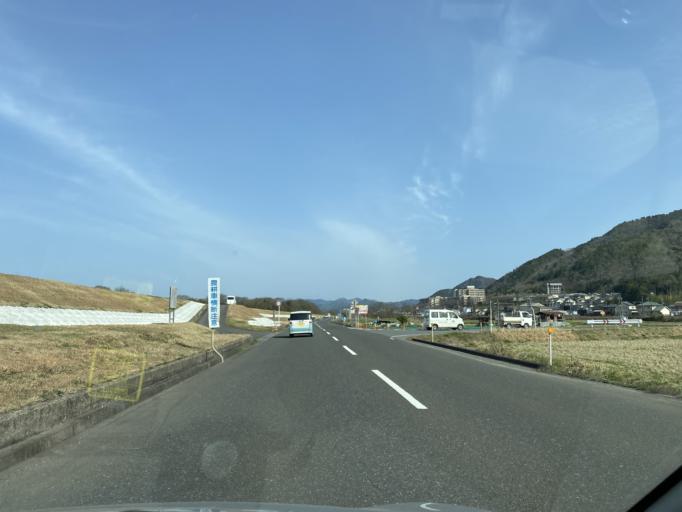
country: JP
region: Kyoto
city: Ayabe
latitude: 35.3067
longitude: 135.2082
